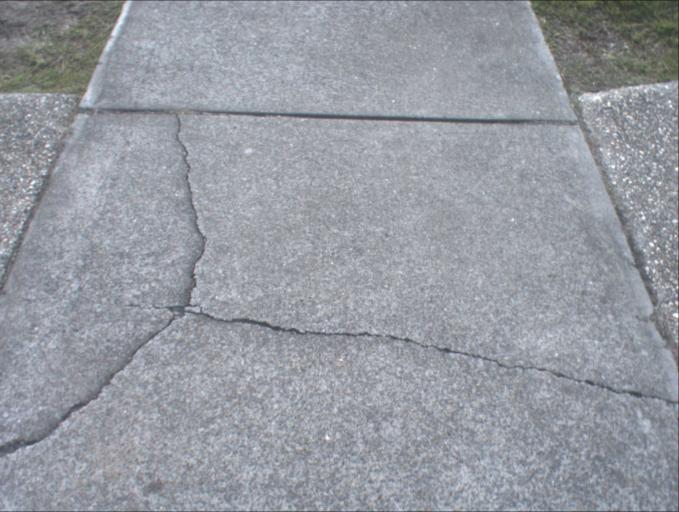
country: AU
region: Queensland
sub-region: Logan
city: Waterford West
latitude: -27.7075
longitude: 153.1544
